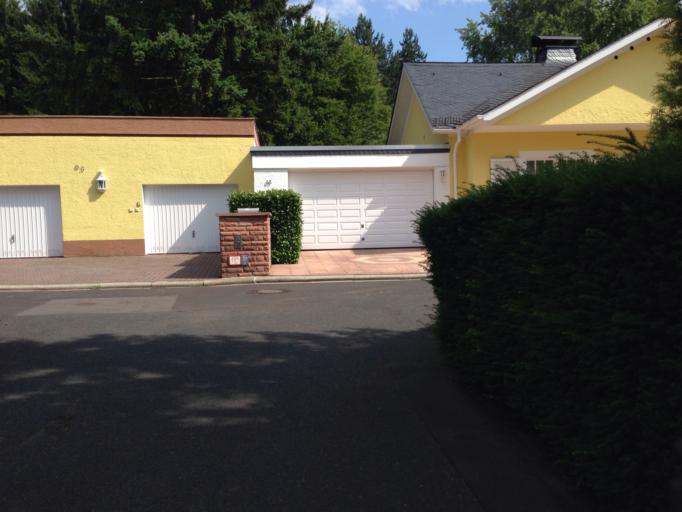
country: DE
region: Hesse
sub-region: Regierungsbezirk Darmstadt
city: Grosskrotzenburg
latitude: 50.1012
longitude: 8.9707
